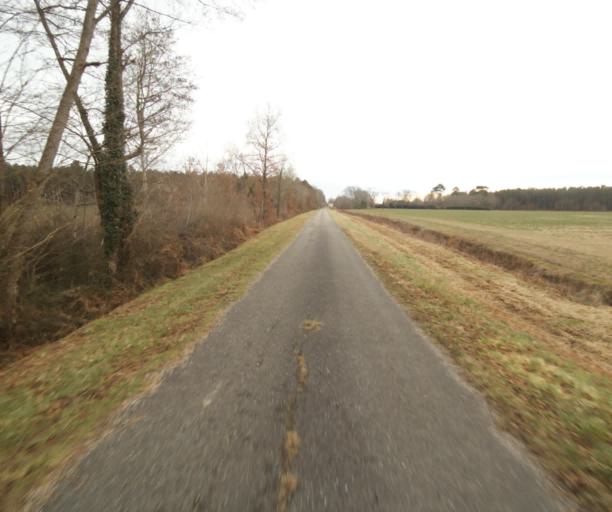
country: FR
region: Aquitaine
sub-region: Departement des Landes
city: Gabarret
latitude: 44.0183
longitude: -0.0405
